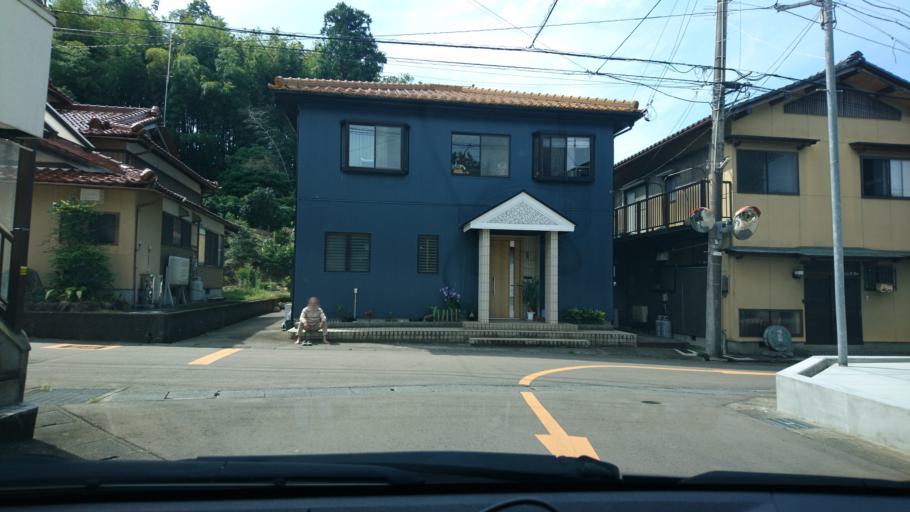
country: JP
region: Ishikawa
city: Komatsu
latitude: 36.3036
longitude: 136.3369
